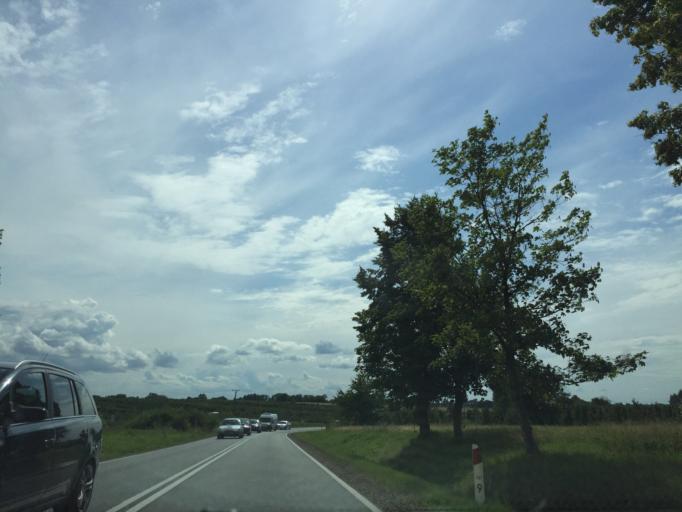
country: PL
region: Masovian Voivodeship
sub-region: Powiat losicki
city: Sarnaki
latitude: 52.3117
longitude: 22.8800
